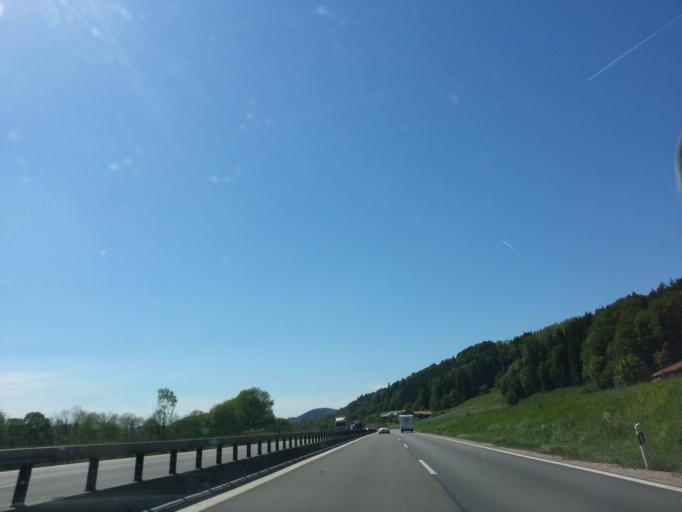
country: DE
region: Bavaria
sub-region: Upper Bavaria
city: Siegsdorf
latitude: 47.8241
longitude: 12.6737
